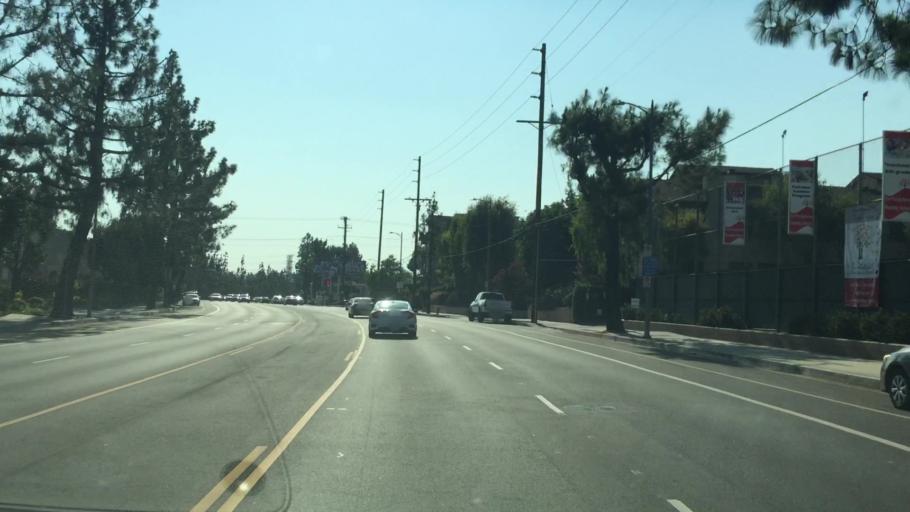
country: US
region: California
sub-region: Los Angeles County
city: Northridge
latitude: 34.2576
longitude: -118.5211
